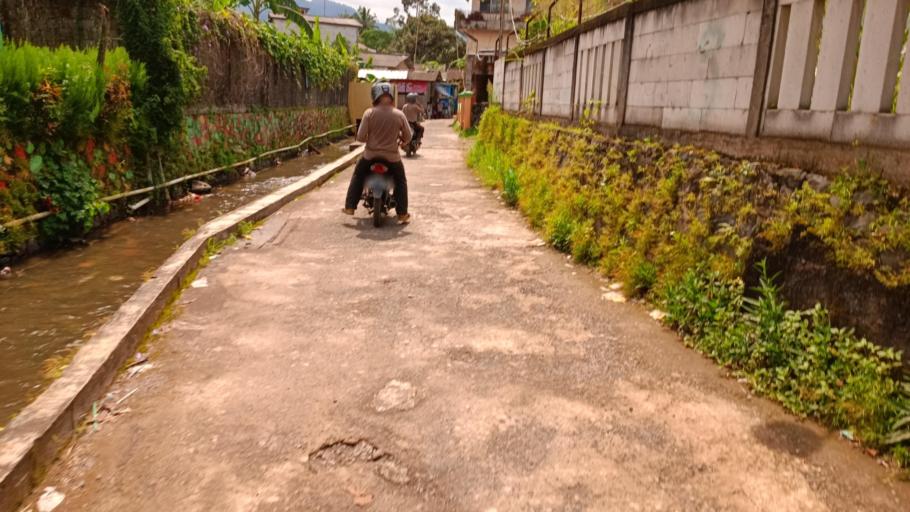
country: ID
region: West Java
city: Caringin
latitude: -6.6527
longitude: 106.8952
